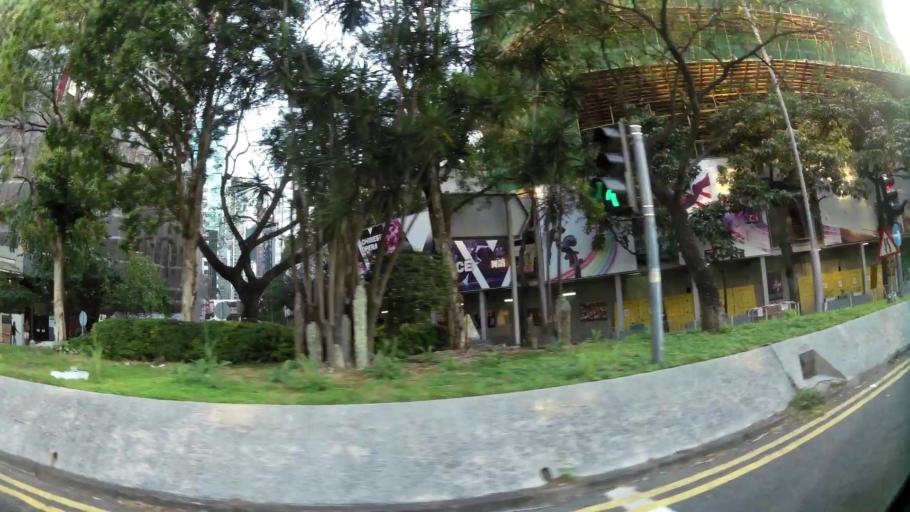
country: HK
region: Wanchai
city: Wan Chai
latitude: 22.2806
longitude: 114.1706
